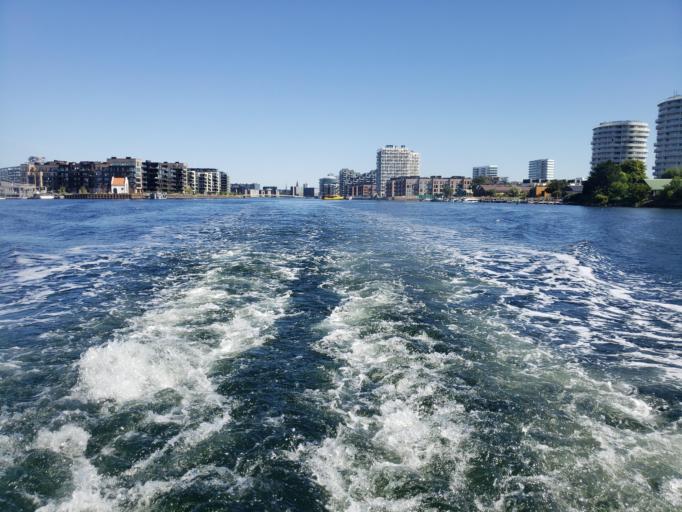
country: DK
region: Capital Region
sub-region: Kobenhavn
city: Copenhagen
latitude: 55.6523
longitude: 12.5599
